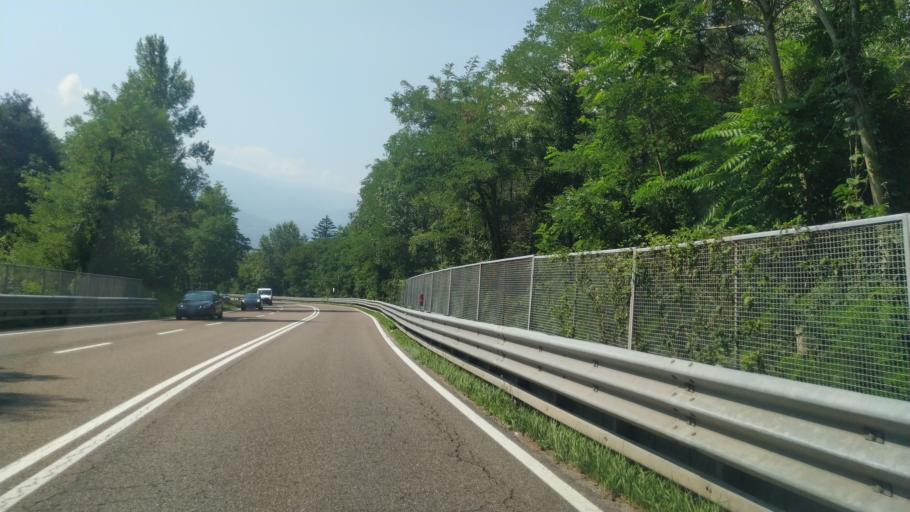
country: IT
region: Trentino-Alto Adige
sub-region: Provincia di Trento
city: Denno
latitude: 46.2838
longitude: 11.0623
